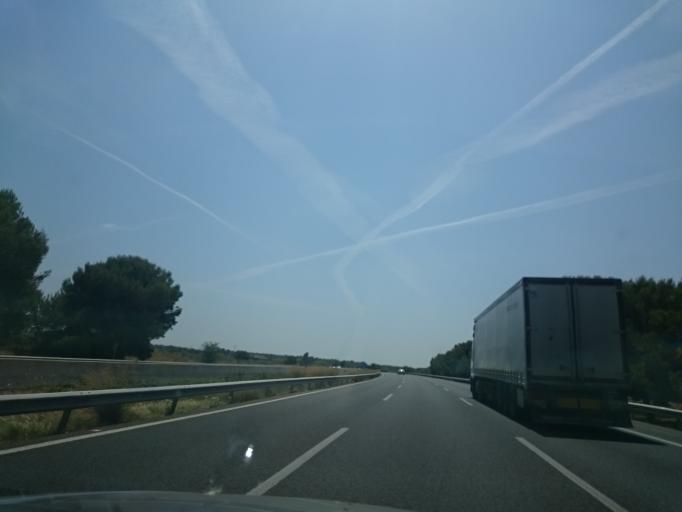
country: ES
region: Catalonia
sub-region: Provincia de Tarragona
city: Sant Jaume dels Domenys
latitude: 41.2995
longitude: 1.6022
